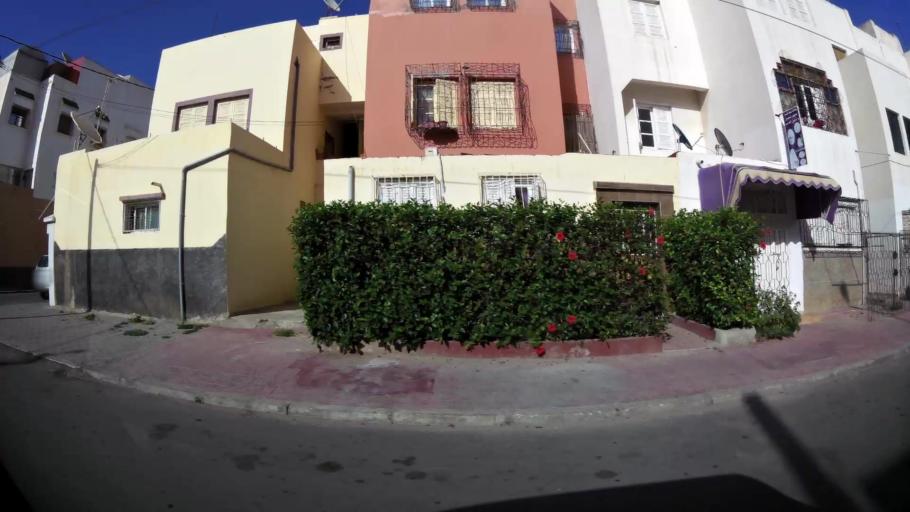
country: MA
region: Souss-Massa-Draa
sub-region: Inezgane-Ait Mellou
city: Inezgane
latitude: 30.3670
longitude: -9.5287
